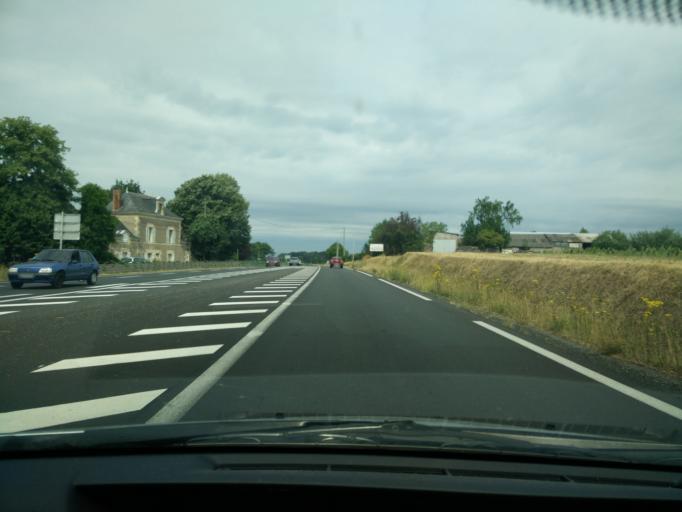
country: FR
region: Pays de la Loire
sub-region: Departement de Maine-et-Loire
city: Brissac-Quince
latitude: 47.3644
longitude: -0.4512
